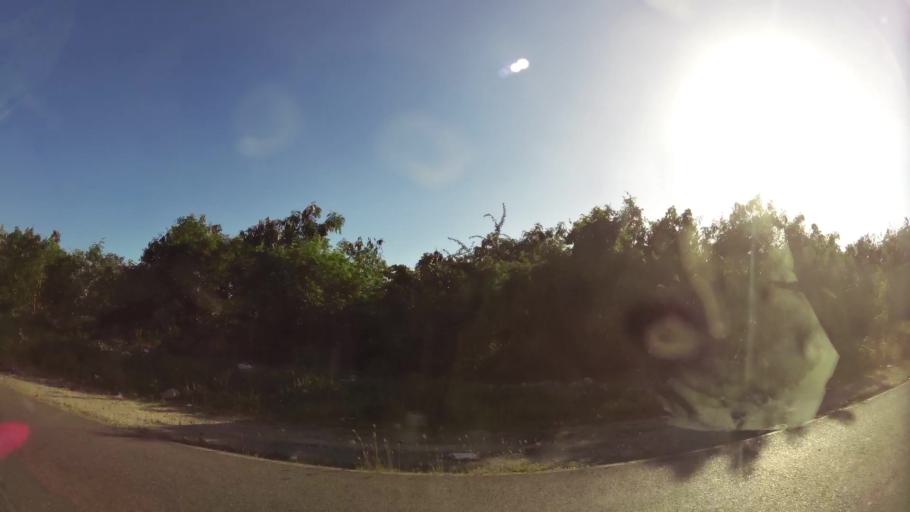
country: DO
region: Santo Domingo
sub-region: Santo Domingo
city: Santo Domingo Este
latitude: 18.4840
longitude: -69.8169
